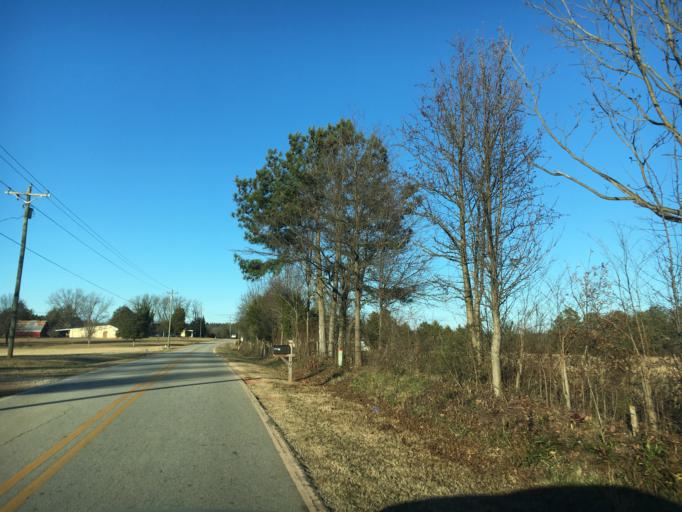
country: US
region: Georgia
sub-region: Hart County
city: Hartwell
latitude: 34.3787
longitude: -83.0266
